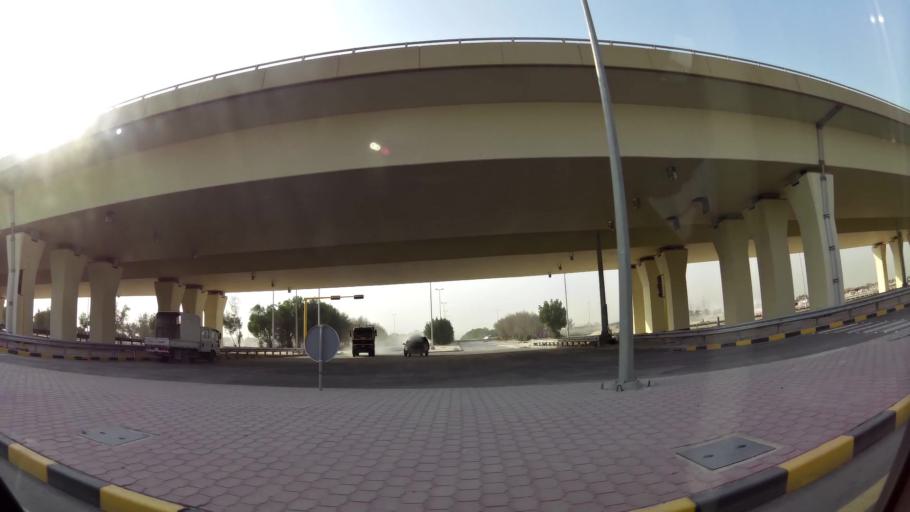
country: KW
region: Al Asimah
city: Ar Rabiyah
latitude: 29.3114
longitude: 47.8321
